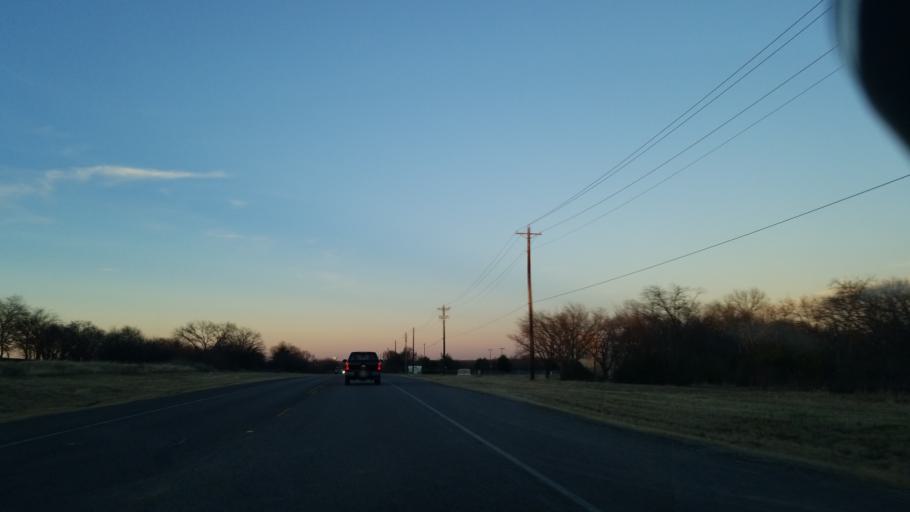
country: US
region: Texas
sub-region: Denton County
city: Argyle
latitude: 33.1386
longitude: -97.1750
